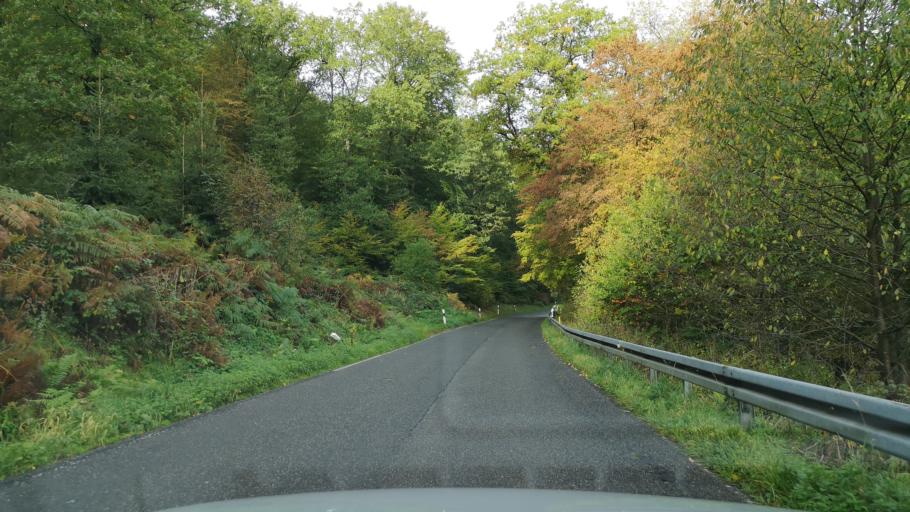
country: DE
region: North Rhine-Westphalia
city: Hattingen
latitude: 51.3603
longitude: 7.1533
